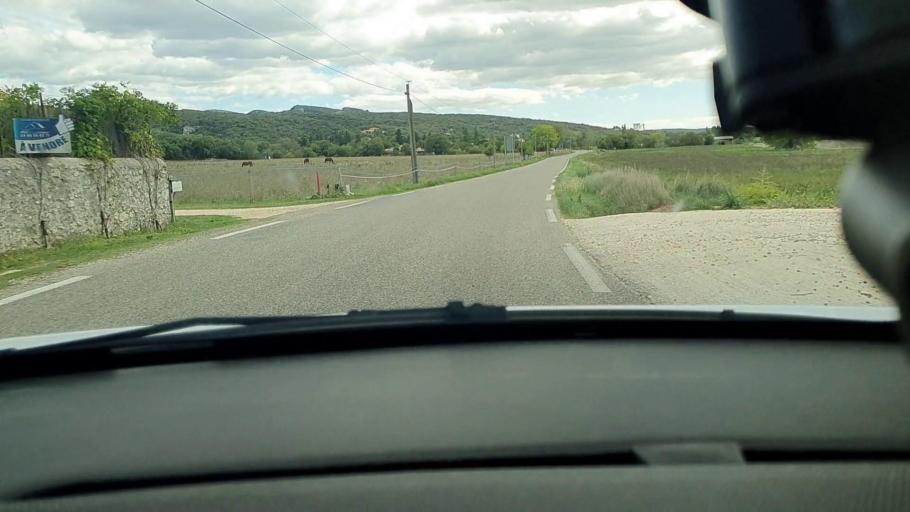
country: FR
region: Languedoc-Roussillon
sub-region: Departement du Gard
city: Salindres
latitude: 44.1830
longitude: 4.2349
